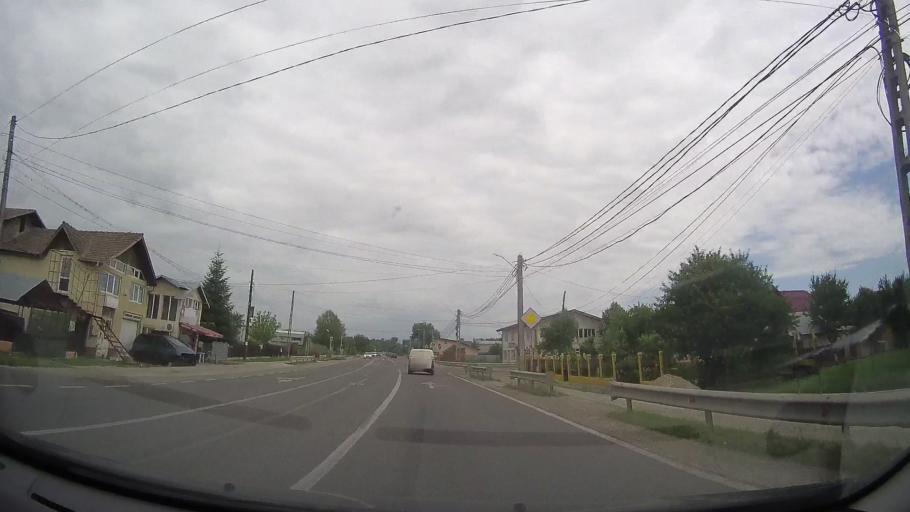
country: RO
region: Prahova
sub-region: Comuna Blejoiu
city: Blejoi
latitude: 45.0036
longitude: 26.0183
